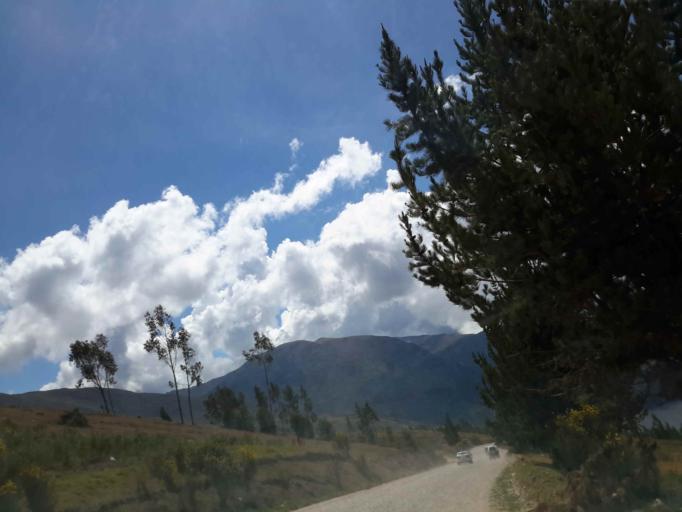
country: PE
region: Apurimac
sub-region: Provincia de Andahuaylas
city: Pacucha
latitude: -13.6231
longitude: -73.3382
